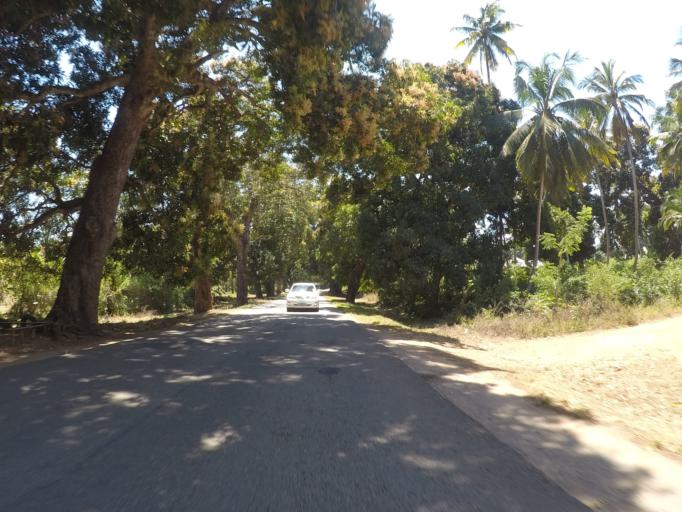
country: TZ
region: Zanzibar Central/South
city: Koani
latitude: -6.2657
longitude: 39.3425
